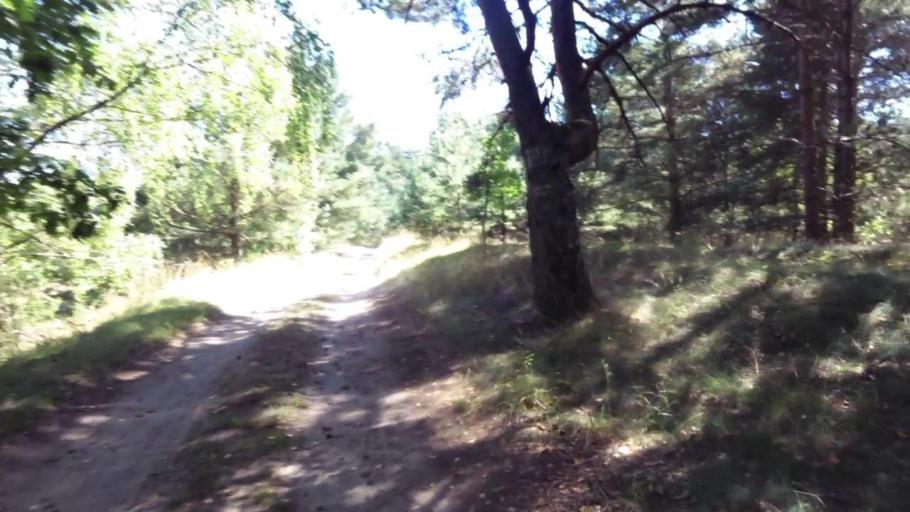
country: PL
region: West Pomeranian Voivodeship
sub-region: Powiat szczecinecki
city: Bialy Bor
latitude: 53.8383
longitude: 16.8738
